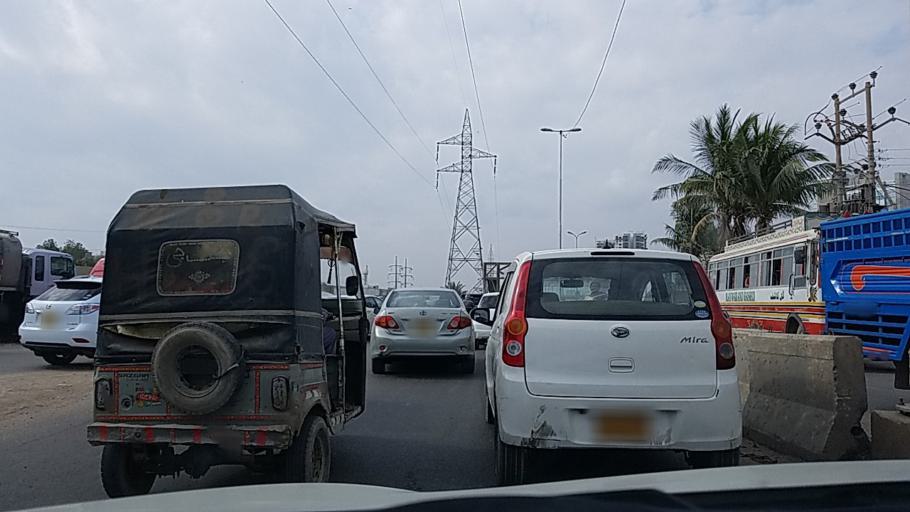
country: PK
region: Sindh
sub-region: Karachi District
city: Karachi
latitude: 24.8275
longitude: 67.0846
